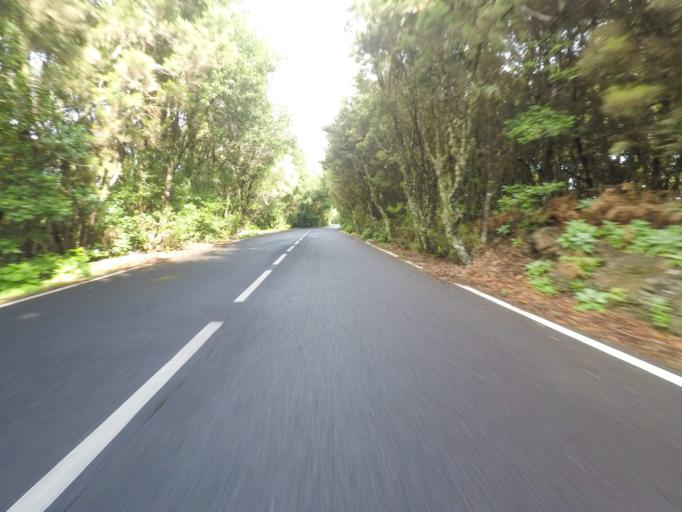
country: ES
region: Canary Islands
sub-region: Provincia de Santa Cruz de Tenerife
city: Alajero
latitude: 28.1160
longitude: -17.2185
